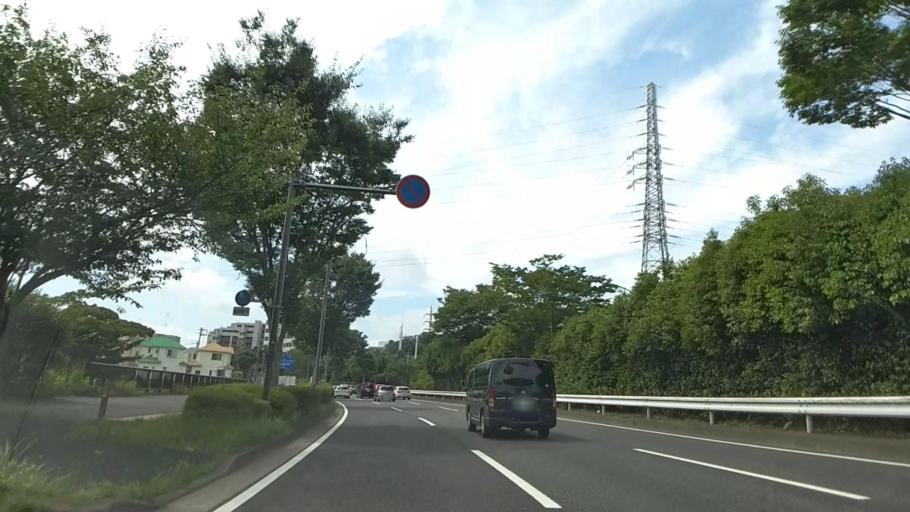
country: JP
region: Kanagawa
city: Yokohama
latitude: 35.4386
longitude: 139.5605
